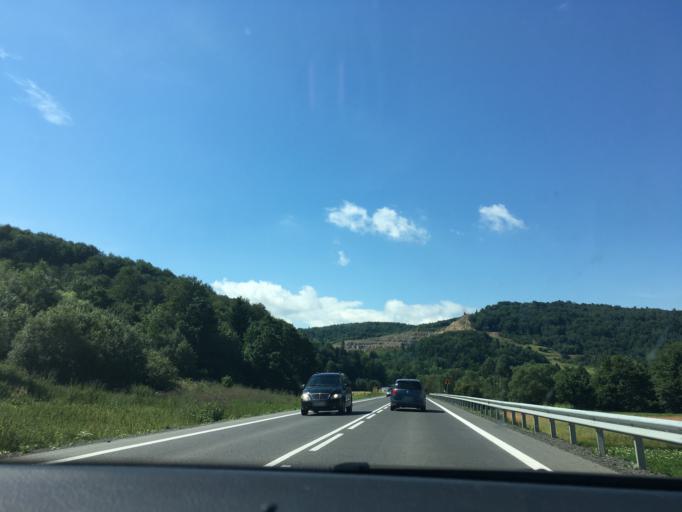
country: PL
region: Subcarpathian Voivodeship
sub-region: Powiat krosnienski
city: Dukla
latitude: 49.5201
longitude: 21.6916
